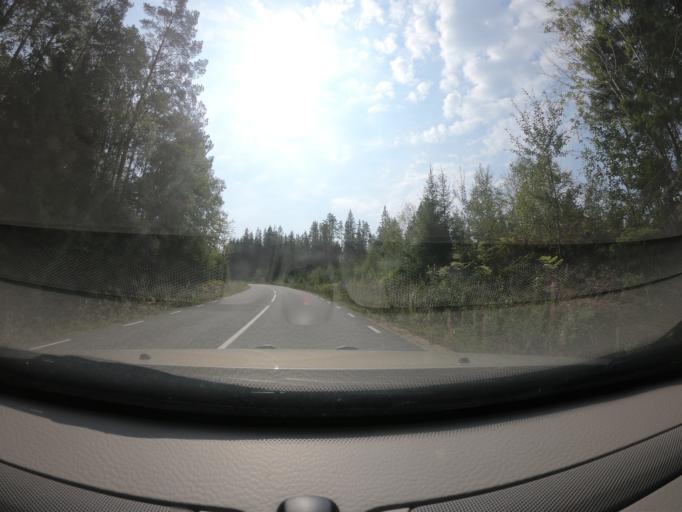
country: SE
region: Joenkoeping
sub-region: Vetlanda Kommun
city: Landsbro
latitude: 57.2577
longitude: 14.9347
